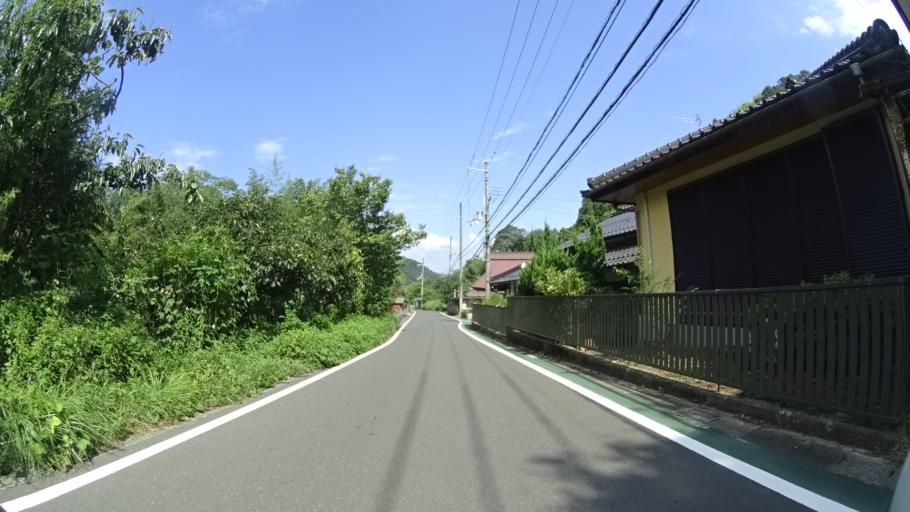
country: JP
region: Kyoto
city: Maizuru
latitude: 35.4302
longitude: 135.3004
